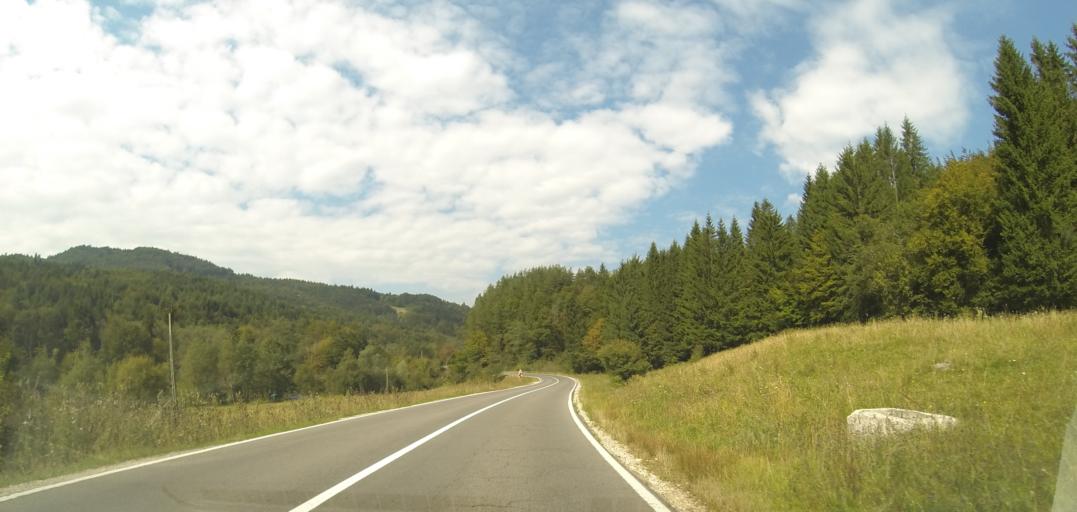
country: RO
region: Brasov
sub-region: Comuna Tarlungeni
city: Zizin
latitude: 45.5428
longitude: 25.8254
